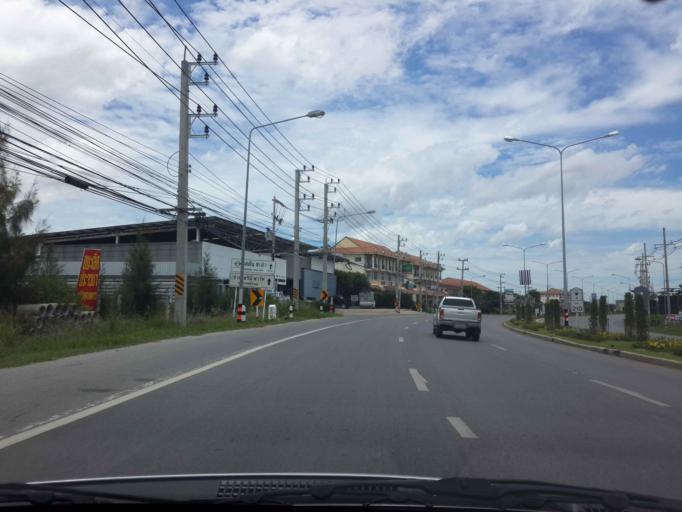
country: TH
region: Prachuap Khiri Khan
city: Hua Hin
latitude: 12.6347
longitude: 99.9486
